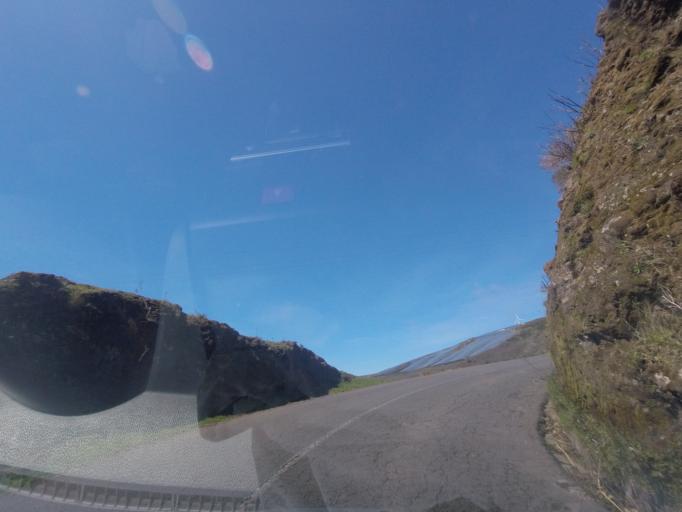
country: PT
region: Madeira
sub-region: Calheta
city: Arco da Calheta
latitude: 32.7347
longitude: -17.1046
